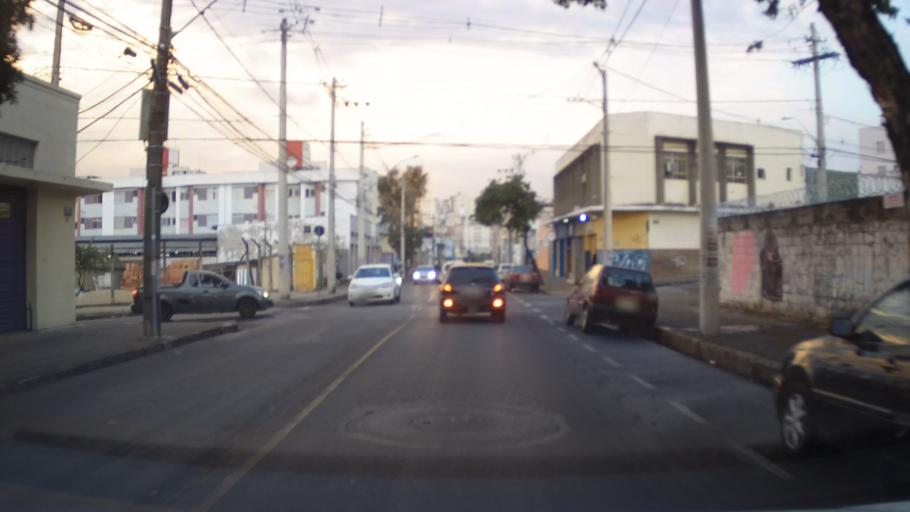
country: BR
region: Minas Gerais
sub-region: Belo Horizonte
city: Belo Horizonte
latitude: -19.9274
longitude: -43.9760
